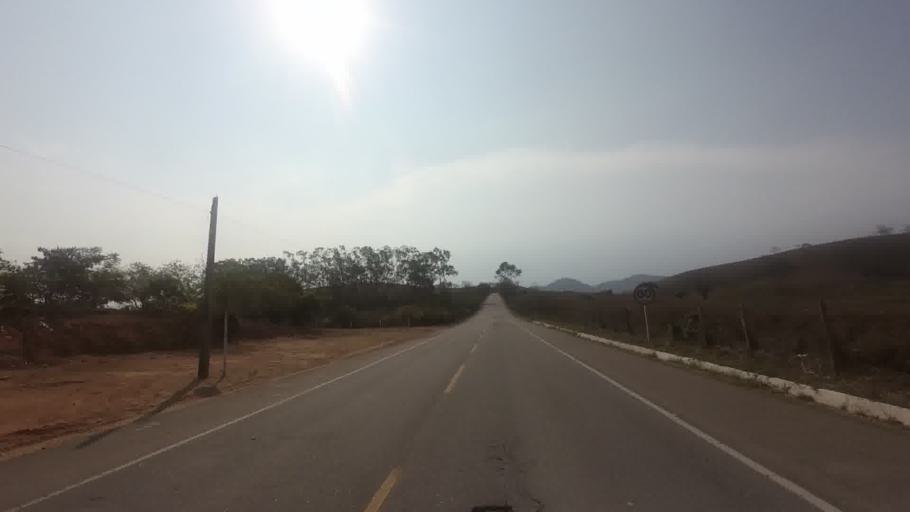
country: BR
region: Rio de Janeiro
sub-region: Bom Jesus Do Itabapoana
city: Bom Jesus do Itabapoana
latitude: -21.1436
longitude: -41.6274
